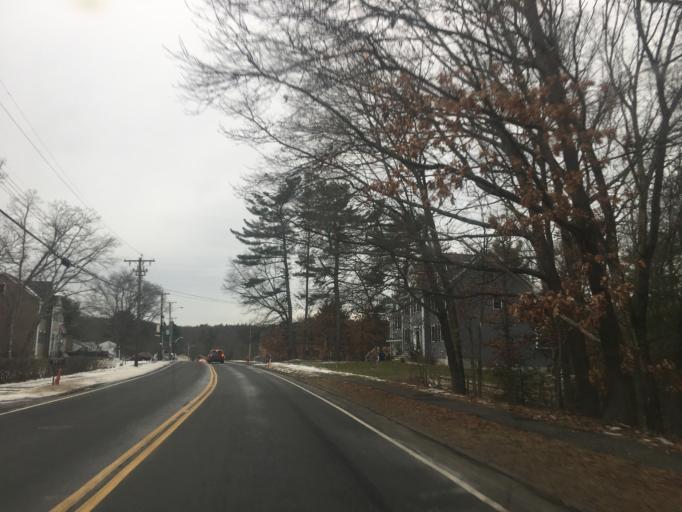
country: US
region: Massachusetts
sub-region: Middlesex County
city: Billerica
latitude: 42.5732
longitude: -71.2882
